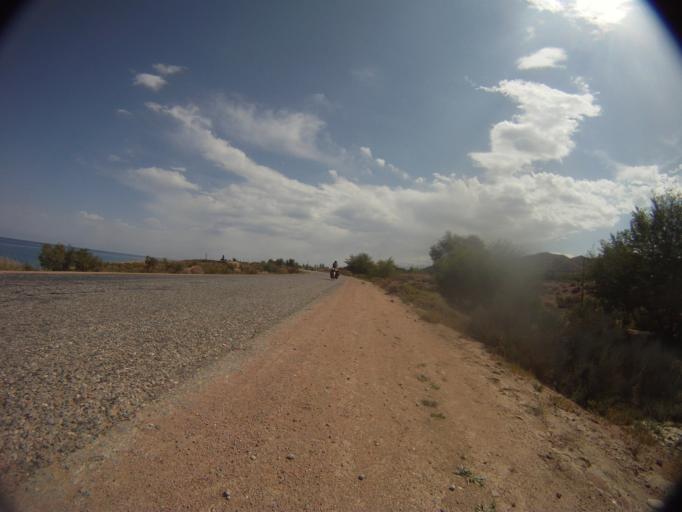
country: KG
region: Ysyk-Koel
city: Kadzhi-Say
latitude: 42.1714
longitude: 77.3759
